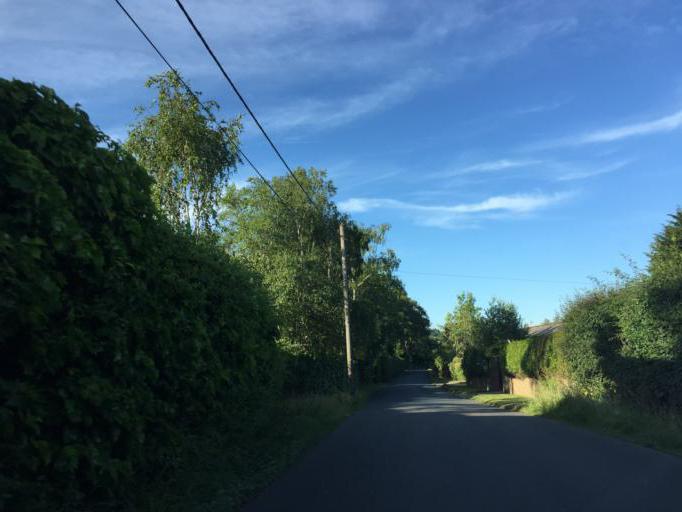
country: GB
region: England
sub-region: East Sussex
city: Wadhurst
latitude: 51.0368
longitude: 0.2890
